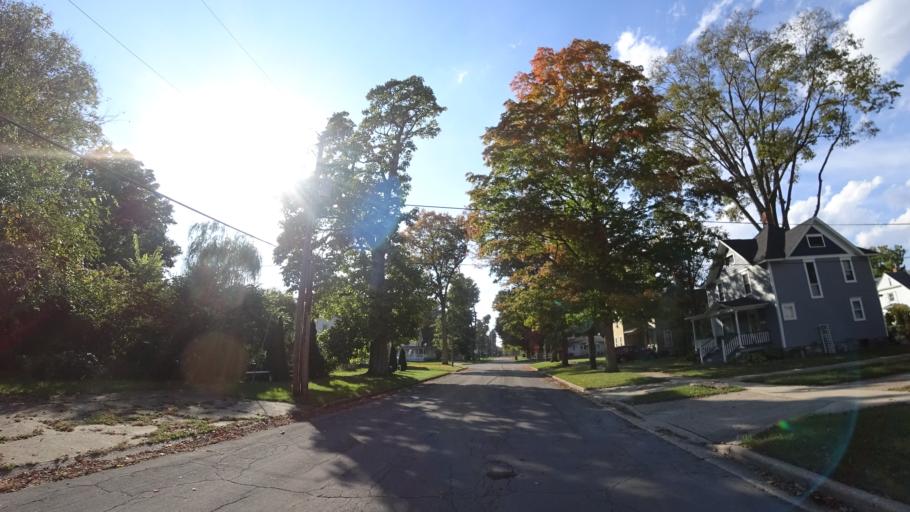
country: US
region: Michigan
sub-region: Saint Joseph County
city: Three Rivers
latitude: 41.9524
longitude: -85.6338
